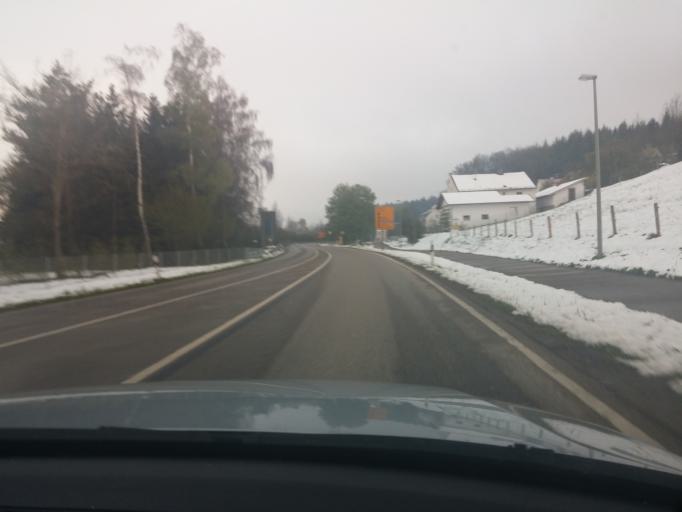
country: DE
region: Bavaria
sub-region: Swabia
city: Memmingen
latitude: 47.9604
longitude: 10.1827
